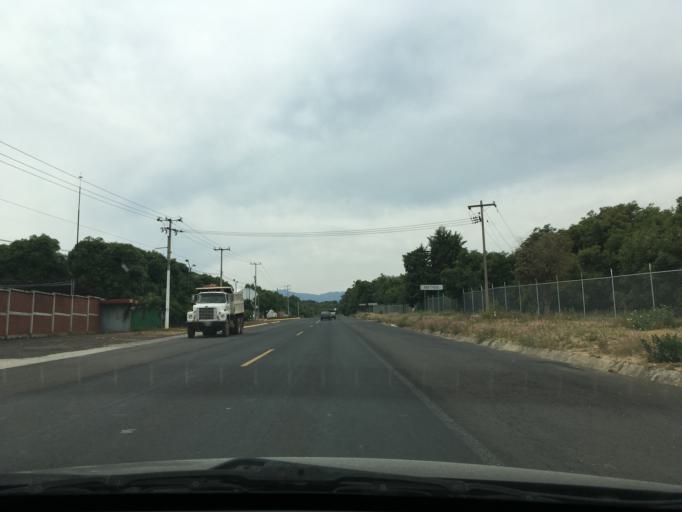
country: MX
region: Michoacan
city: Nuevo San Juan Parangaricutiro
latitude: 19.3926
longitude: -102.1005
